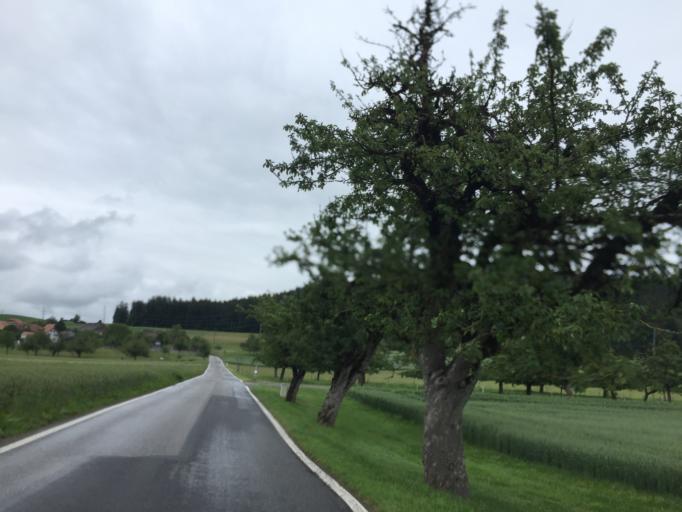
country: CH
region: Bern
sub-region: Bern-Mittelland District
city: Biglen
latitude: 46.9071
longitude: 7.6127
